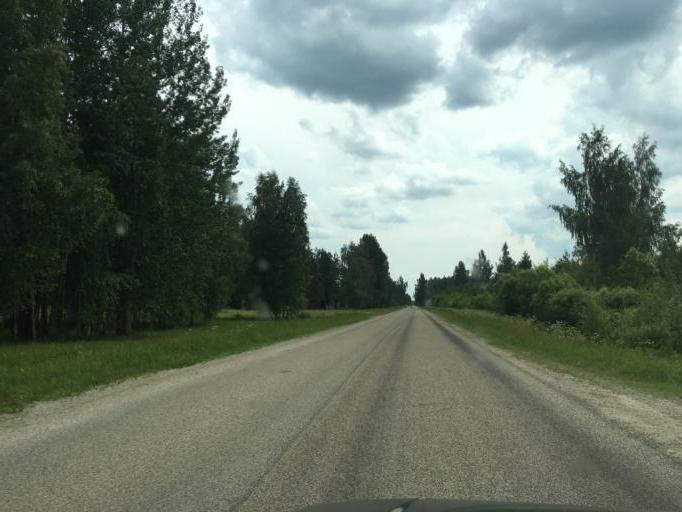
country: LV
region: Rugaju
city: Rugaji
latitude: 56.8321
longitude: 27.0938
